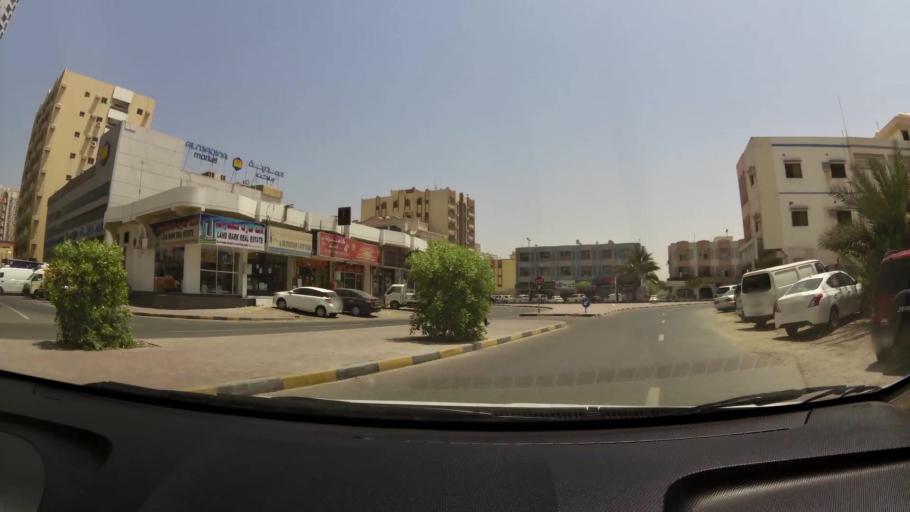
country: AE
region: Ajman
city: Ajman
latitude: 25.3989
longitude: 55.4498
